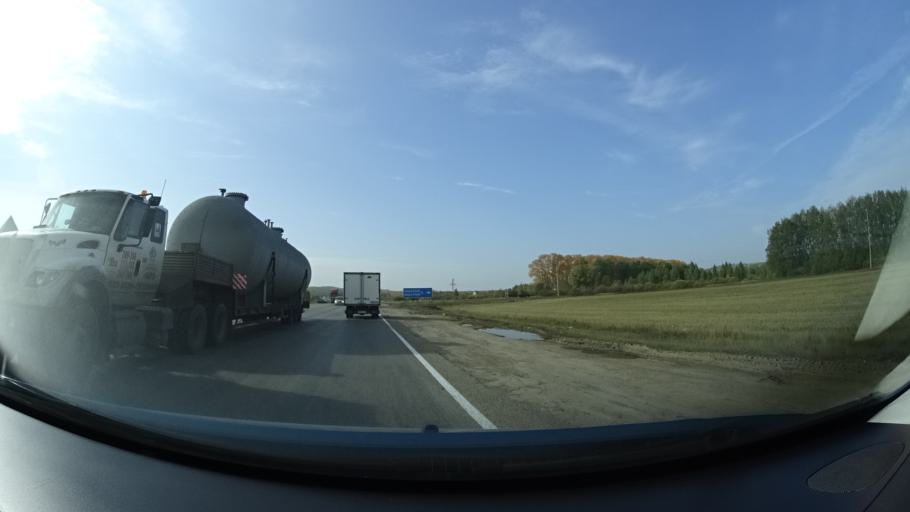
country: RU
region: Bashkortostan
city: Kandry
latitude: 54.6066
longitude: 54.3043
